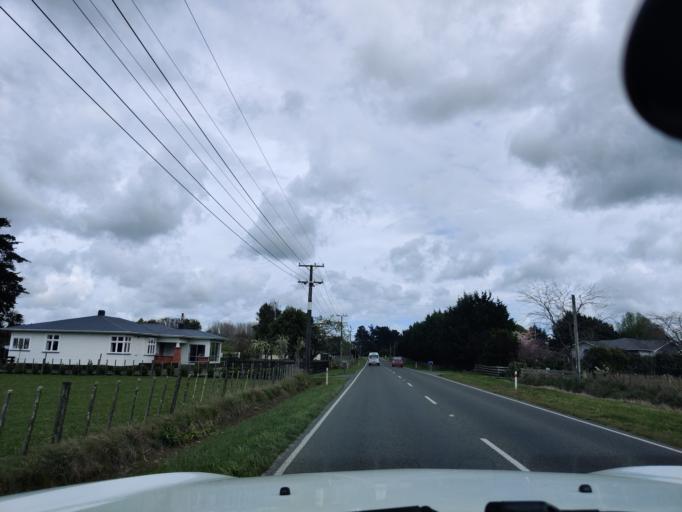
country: NZ
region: Manawatu-Wanganui
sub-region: Palmerston North City
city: Palmerston North
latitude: -40.2402
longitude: 175.5468
